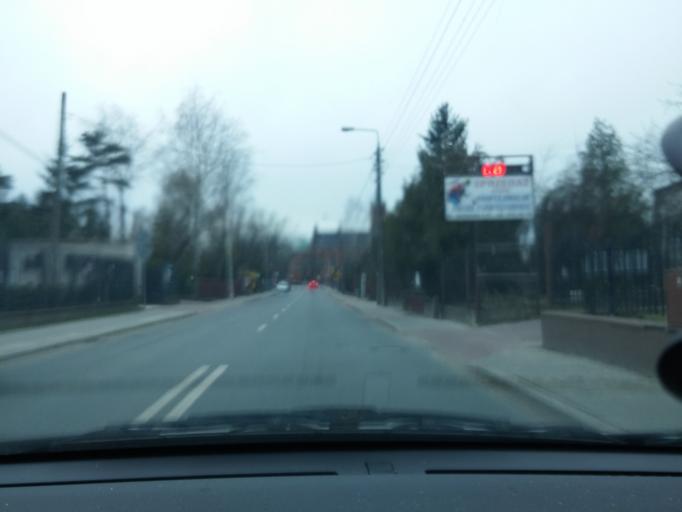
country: PL
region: Masovian Voivodeship
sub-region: Warszawa
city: Wawer
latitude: 52.1973
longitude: 21.1383
